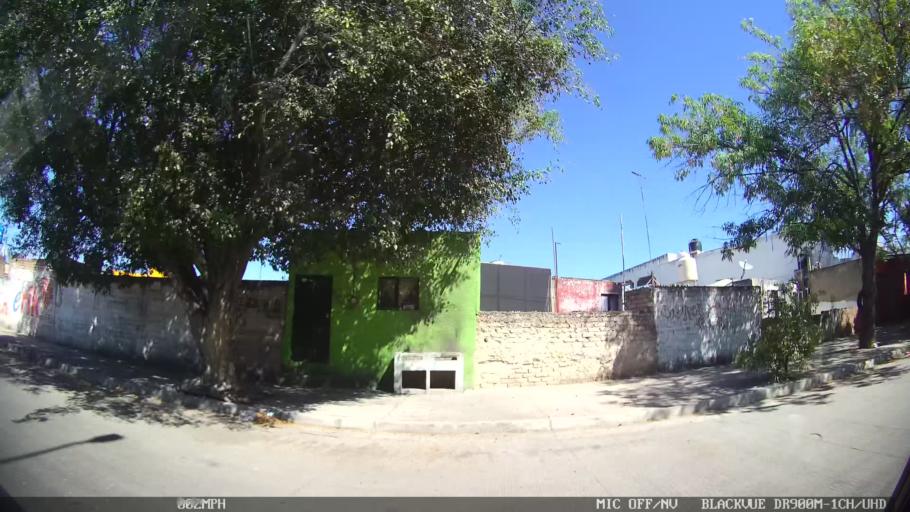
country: MX
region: Jalisco
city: Tlaquepaque
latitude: 20.6999
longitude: -103.2835
